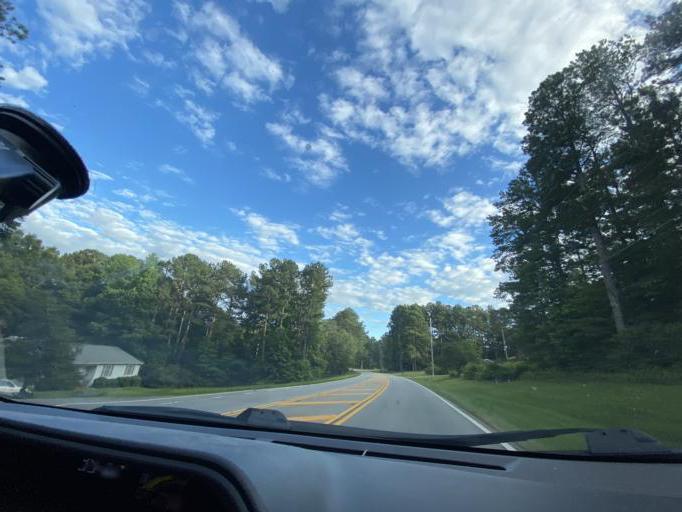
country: US
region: Georgia
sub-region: Fayette County
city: Tyrone
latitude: 33.4505
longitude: -84.6573
